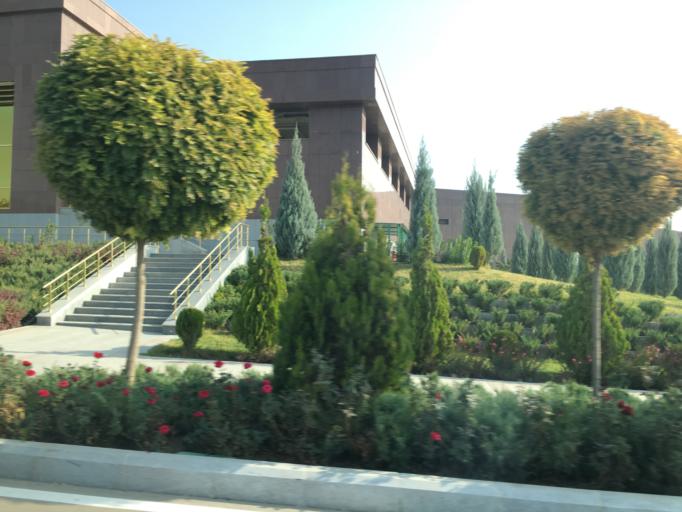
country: TM
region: Ahal
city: Ashgabat
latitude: 37.9363
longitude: 58.3114
